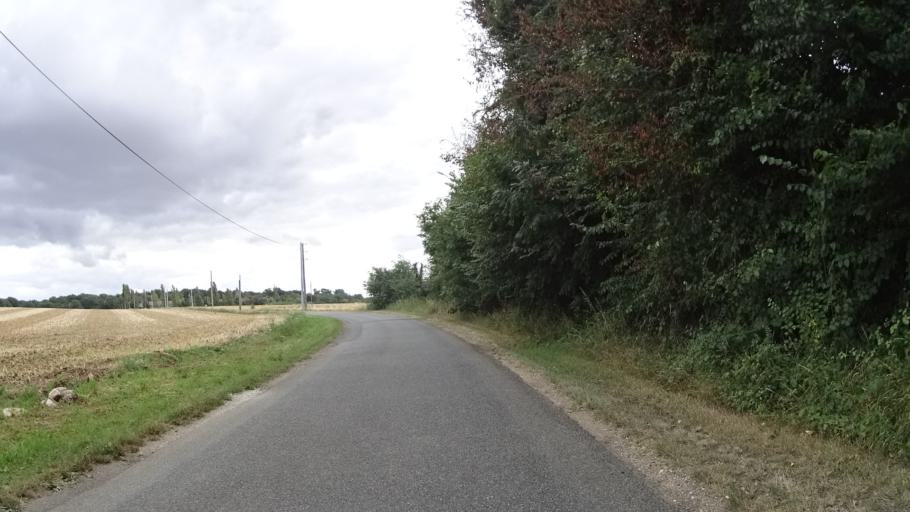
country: FR
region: Centre
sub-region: Departement du Loiret
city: Amilly
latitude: 47.9494
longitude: 2.7969
